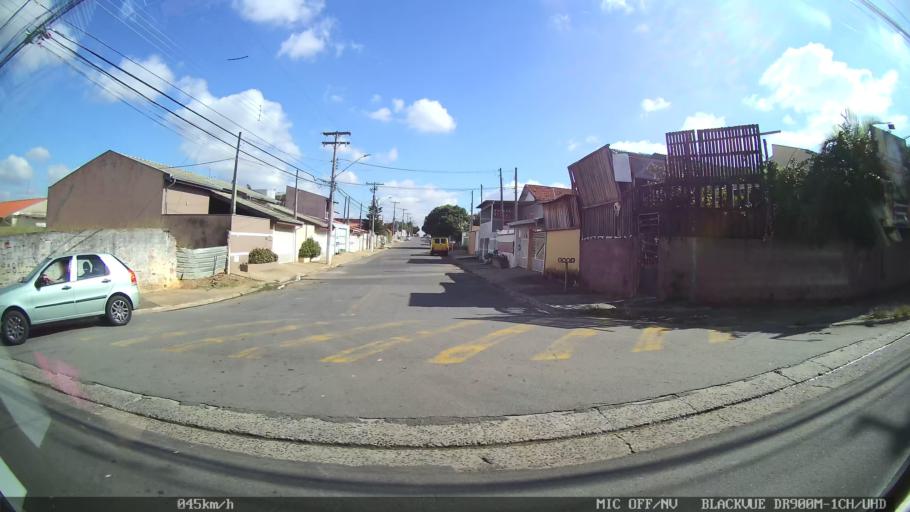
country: BR
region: Sao Paulo
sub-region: Hortolandia
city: Hortolandia
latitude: -22.8862
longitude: -47.2035
